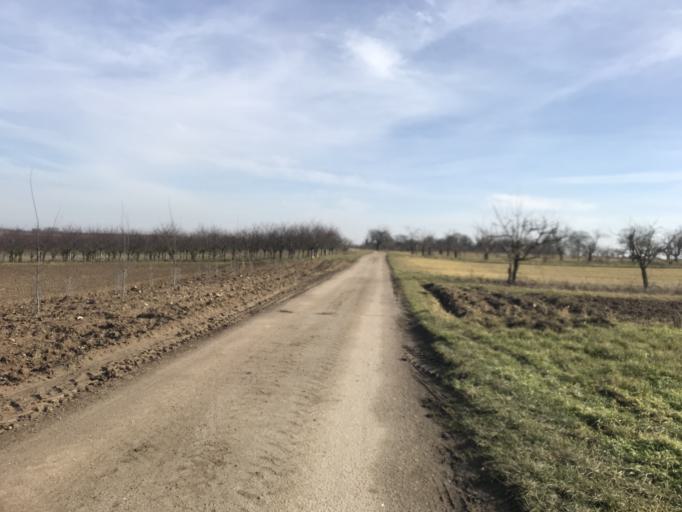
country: DE
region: Rheinland-Pfalz
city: Schwabenheim
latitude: 49.9517
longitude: 8.0909
